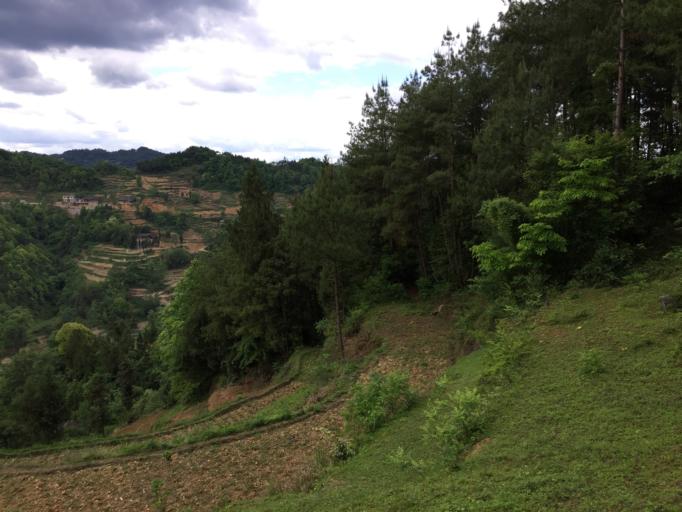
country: CN
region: Guizhou Sheng
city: Xujiaba
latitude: 27.6790
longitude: 108.0868
